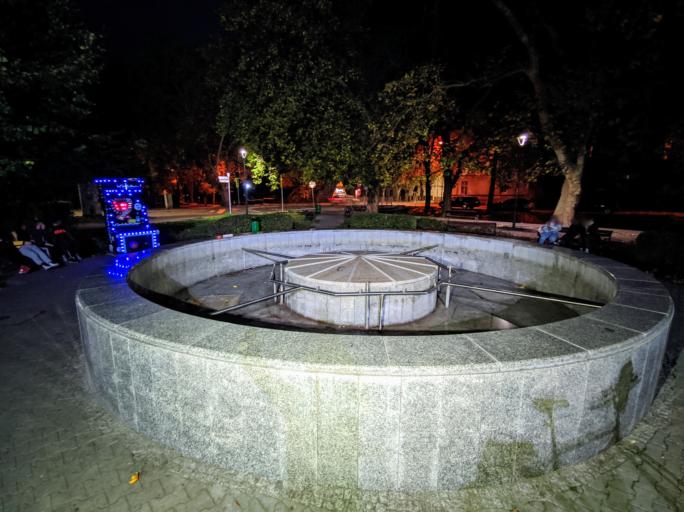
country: PL
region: Lubusz
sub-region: Powiat zarski
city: Lubsko
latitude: 51.7861
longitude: 14.9730
